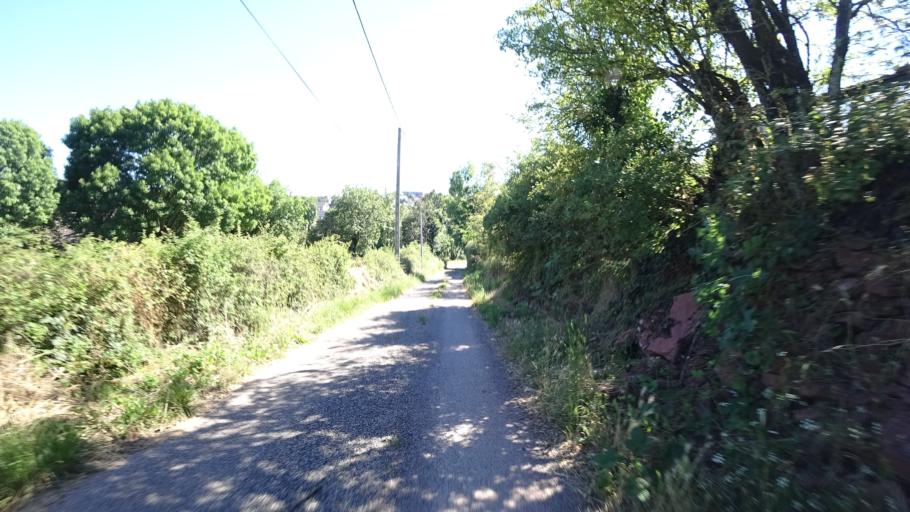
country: FR
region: Midi-Pyrenees
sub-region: Departement de l'Aveyron
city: Rodez
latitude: 44.3665
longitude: 2.5654
